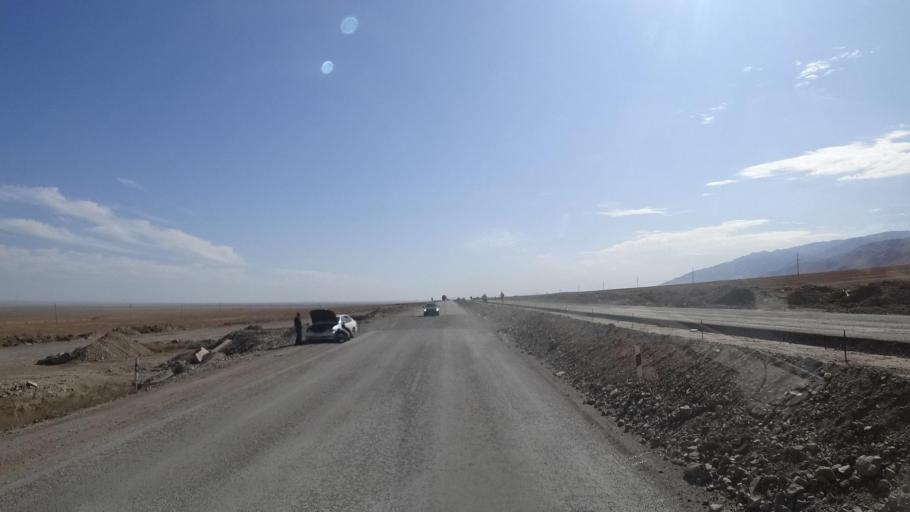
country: KG
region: Chuy
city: Ivanovka
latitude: 43.3837
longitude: 75.1804
